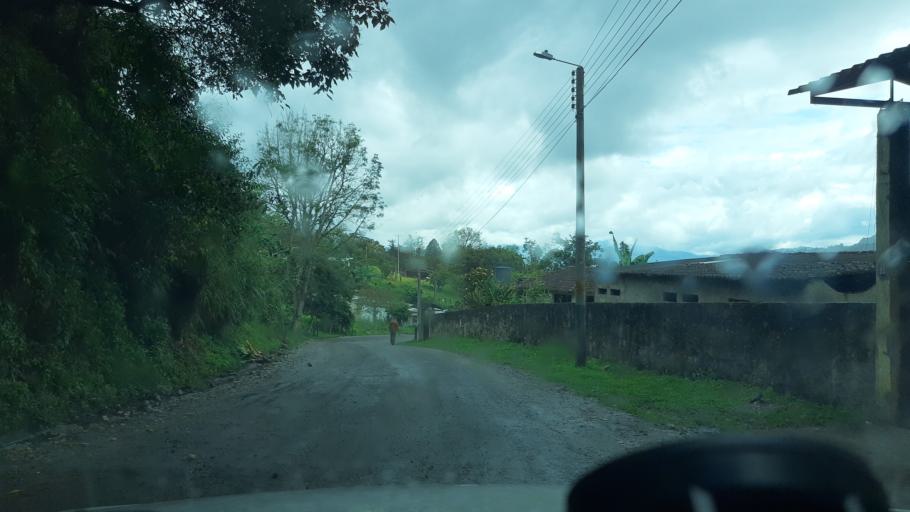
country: CO
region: Boyaca
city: Chinavita
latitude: 5.1641
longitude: -73.3683
